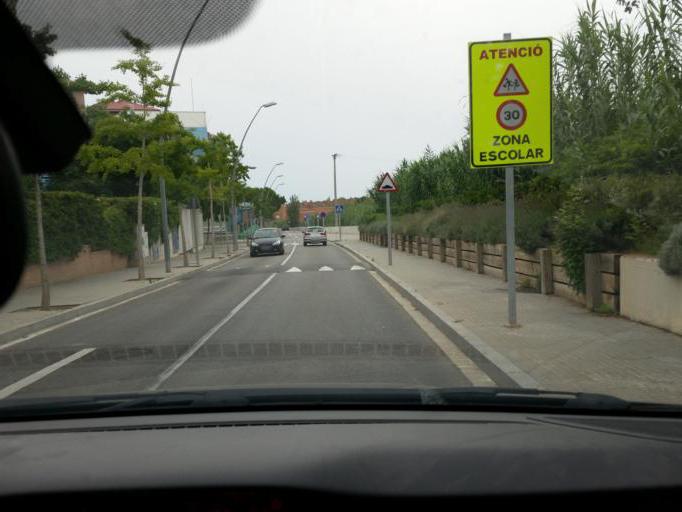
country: ES
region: Catalonia
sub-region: Provincia de Barcelona
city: Vilassar de Mar
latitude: 41.5023
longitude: 2.3815
